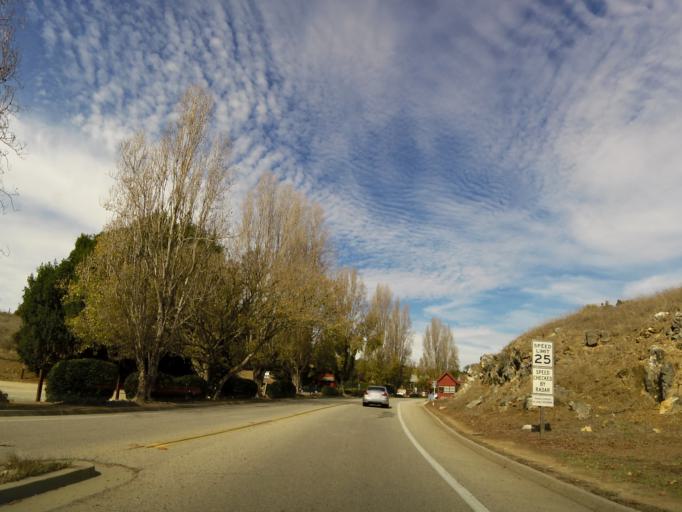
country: US
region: California
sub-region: Santa Cruz County
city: Santa Cruz
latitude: 36.9779
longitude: -122.0539
